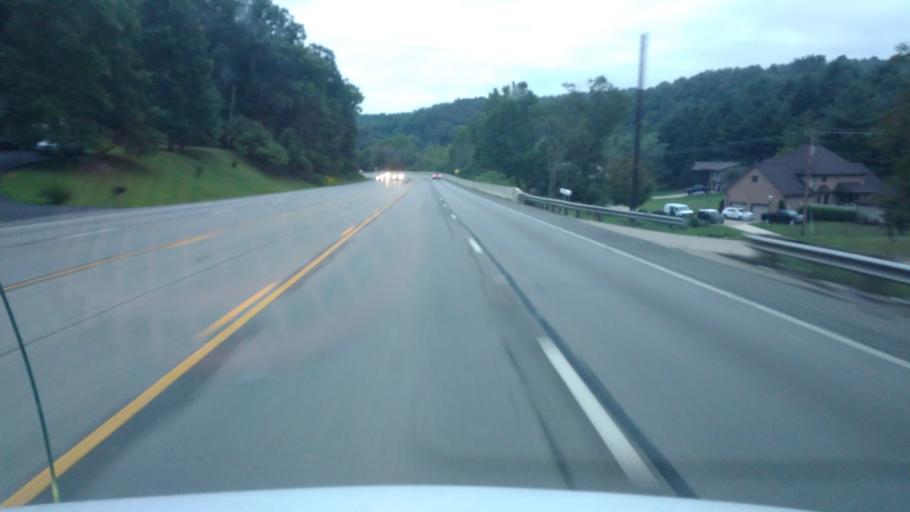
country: US
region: Ohio
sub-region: Pike County
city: Waverly
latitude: 39.2085
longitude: -82.9834
